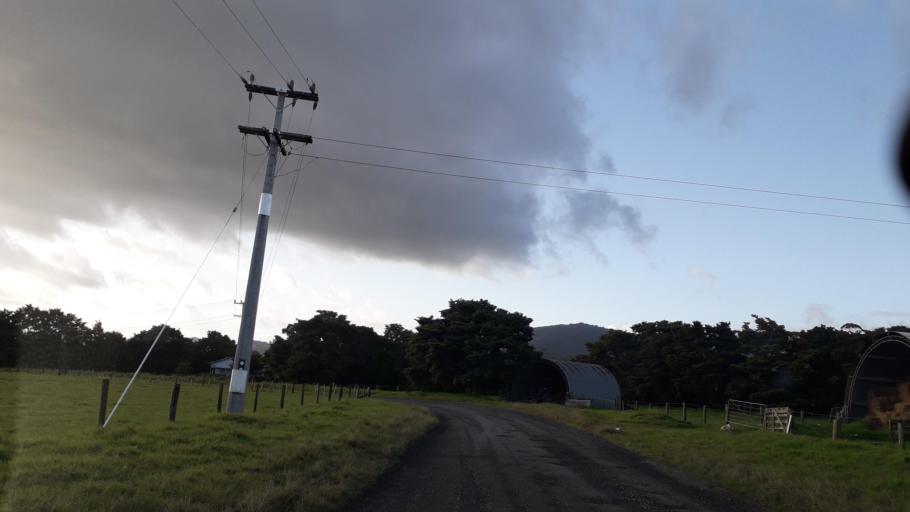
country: NZ
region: Northland
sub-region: Far North District
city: Waimate North
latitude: -35.5031
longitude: 173.6996
